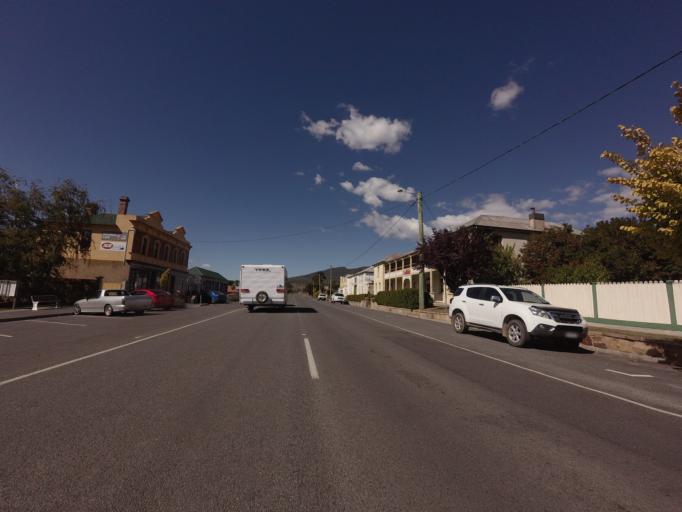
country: AU
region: Tasmania
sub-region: Break O'Day
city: St Helens
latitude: -41.6382
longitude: 147.9704
